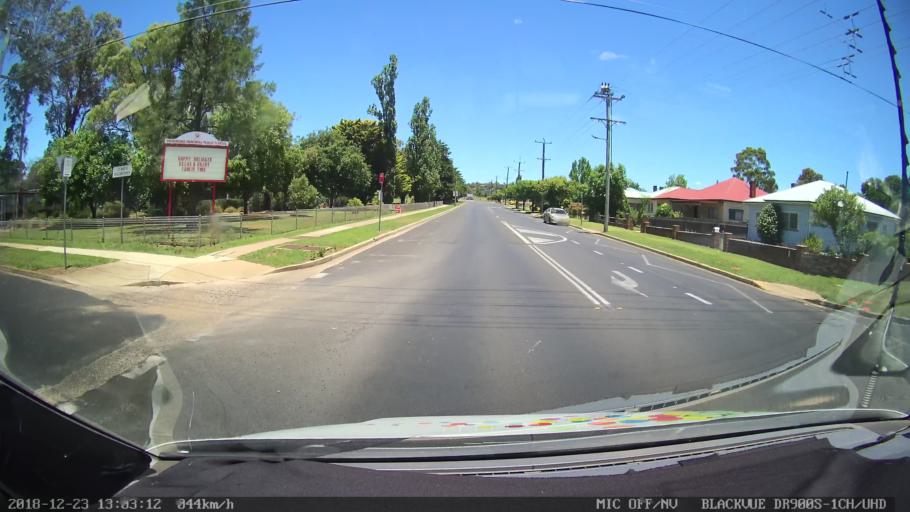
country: AU
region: New South Wales
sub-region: Armidale Dumaresq
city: Armidale
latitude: -30.5102
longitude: 151.6500
